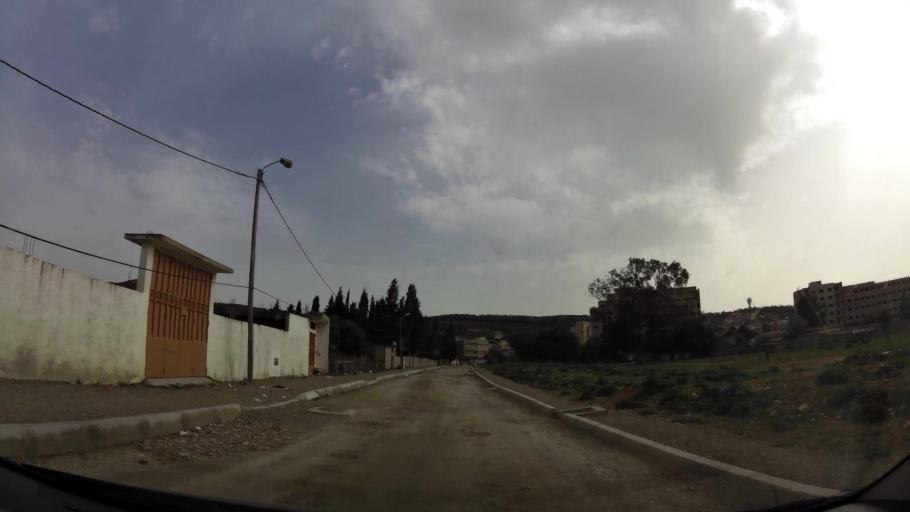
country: MA
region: Tanger-Tetouan
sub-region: Tanger-Assilah
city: Boukhalef
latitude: 35.7063
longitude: -5.9016
